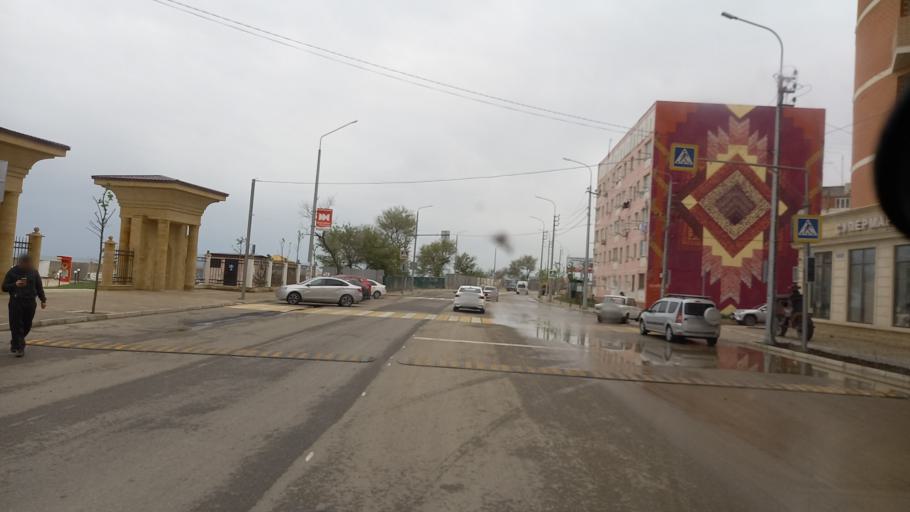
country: RU
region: Dagestan
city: Derbent
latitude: 42.0874
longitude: 48.2921
